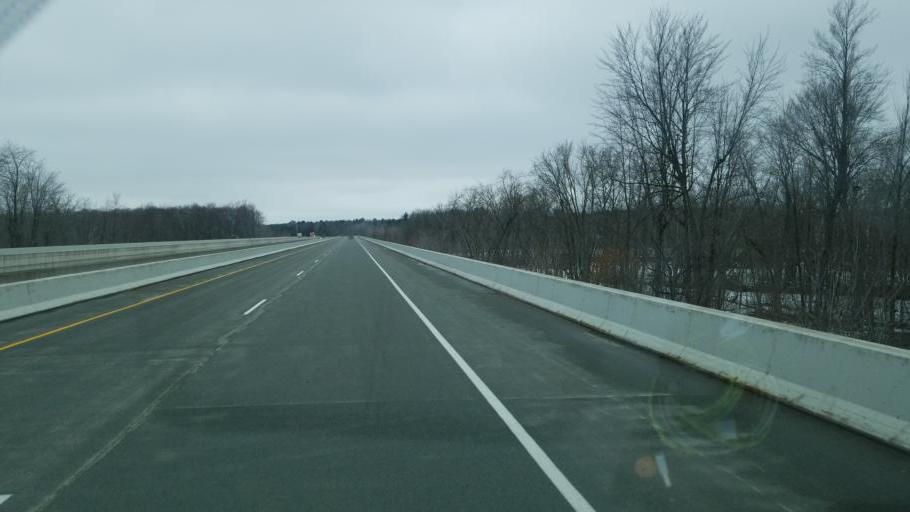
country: US
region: Wisconsin
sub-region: Portage County
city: Stevens Point
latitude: 44.5978
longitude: -89.6421
